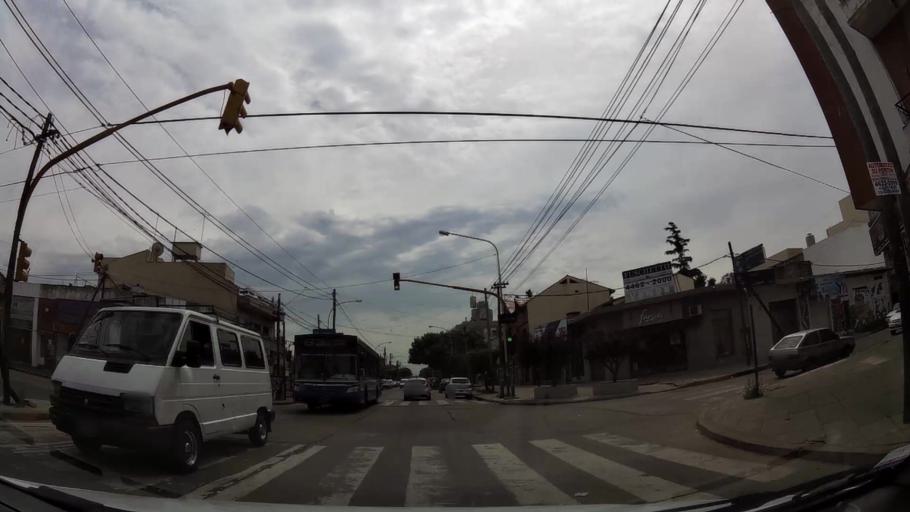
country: AR
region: Buenos Aires F.D.
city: Villa Lugano
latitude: -34.6921
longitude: -58.5003
